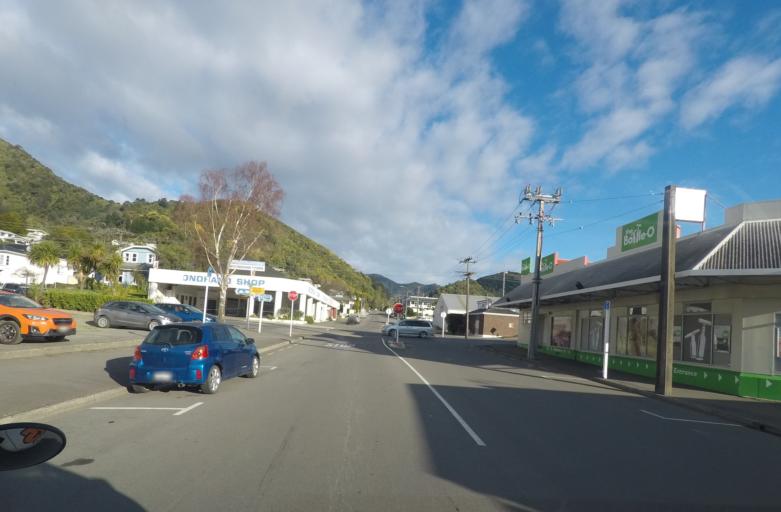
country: NZ
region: Marlborough
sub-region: Marlborough District
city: Picton
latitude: -41.2902
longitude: 174.0080
